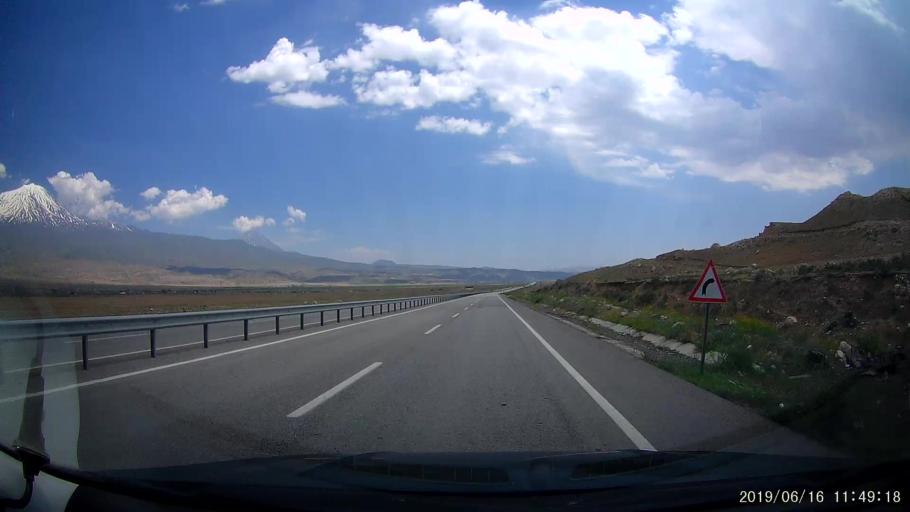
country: TR
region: Agri
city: Dogubayazit
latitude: 39.5575
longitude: 44.1608
